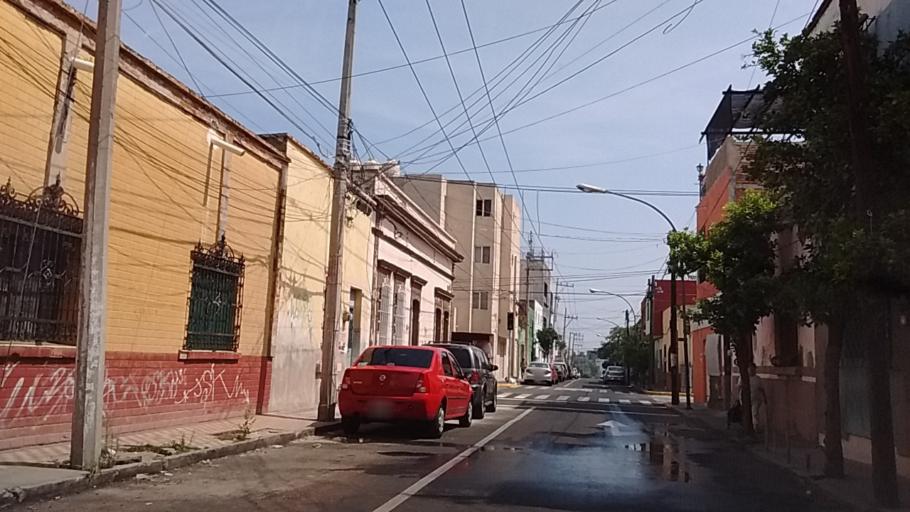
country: MX
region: Jalisco
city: Guadalajara
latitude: 20.6868
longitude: -103.3469
